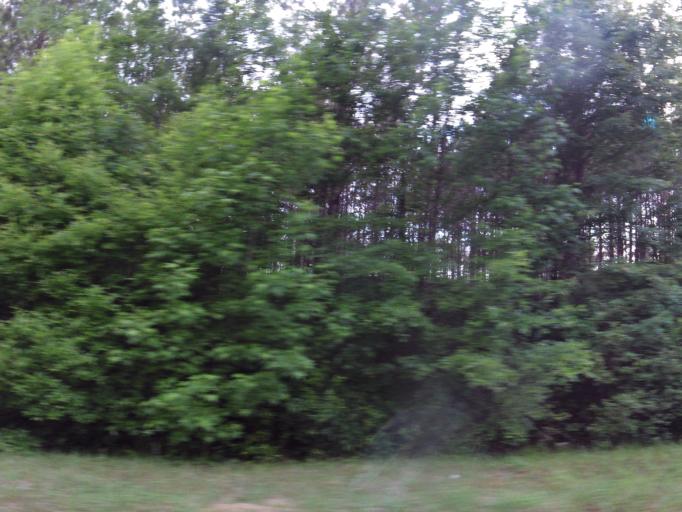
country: US
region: South Carolina
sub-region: Hampton County
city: Estill
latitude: 32.5743
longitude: -81.1872
